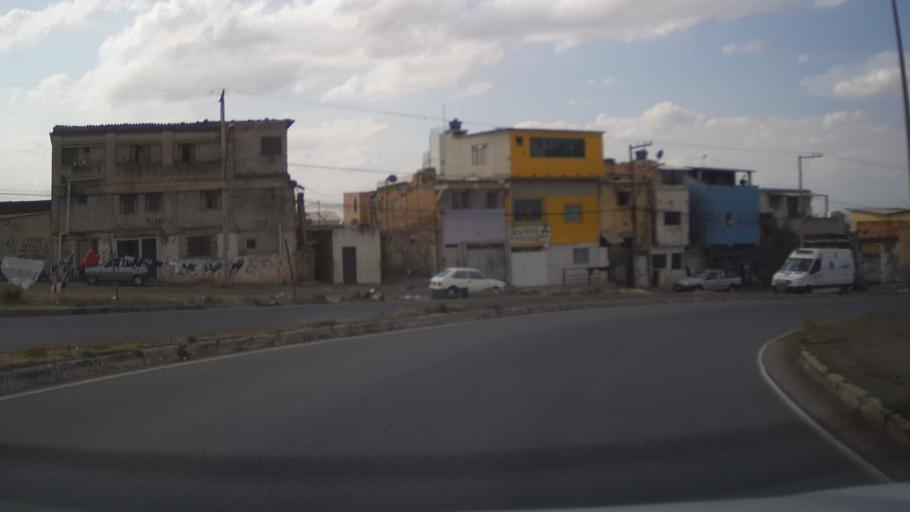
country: BR
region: Minas Gerais
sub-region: Belo Horizonte
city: Belo Horizonte
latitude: -19.8791
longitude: -43.9539
